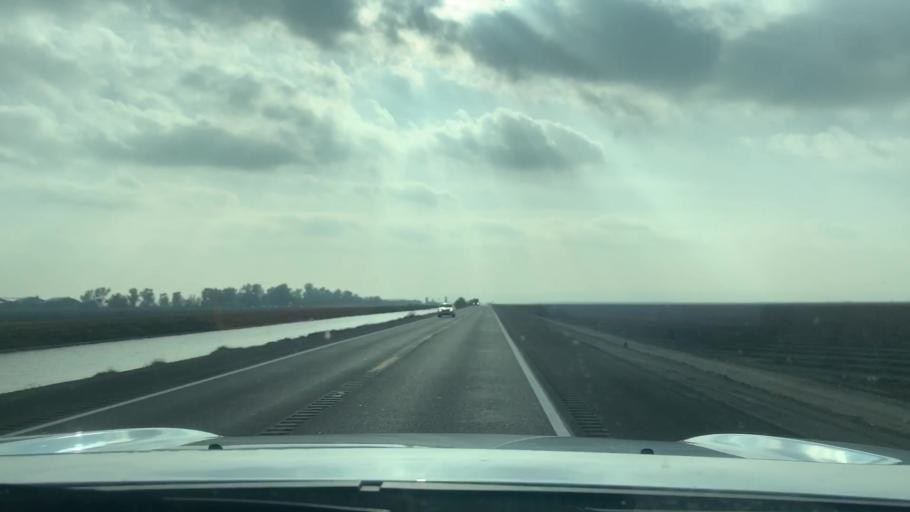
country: US
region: California
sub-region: Kings County
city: Stratford
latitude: 36.1323
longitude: -119.8839
